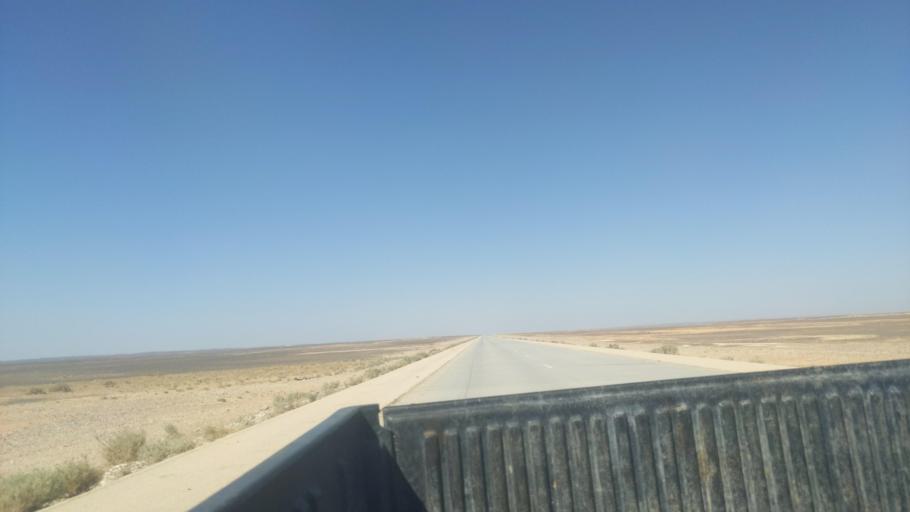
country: JO
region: Amman
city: Al Azraq ash Shamali
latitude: 31.4593
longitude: 36.7913
